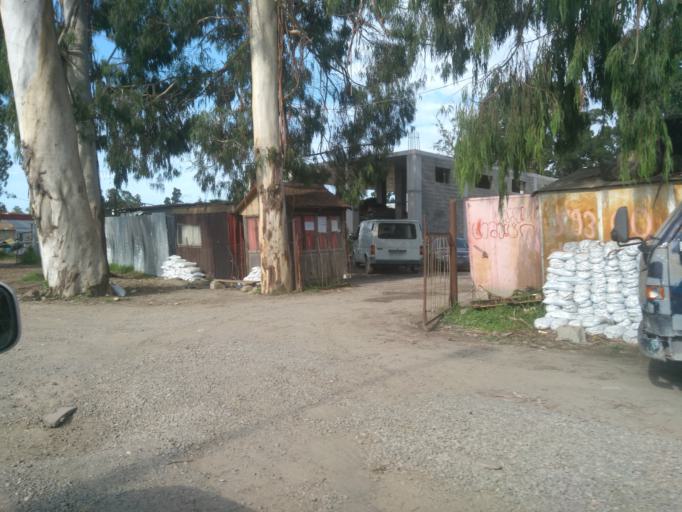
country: GE
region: Ajaria
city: Batumi
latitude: 41.6088
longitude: 41.6266
